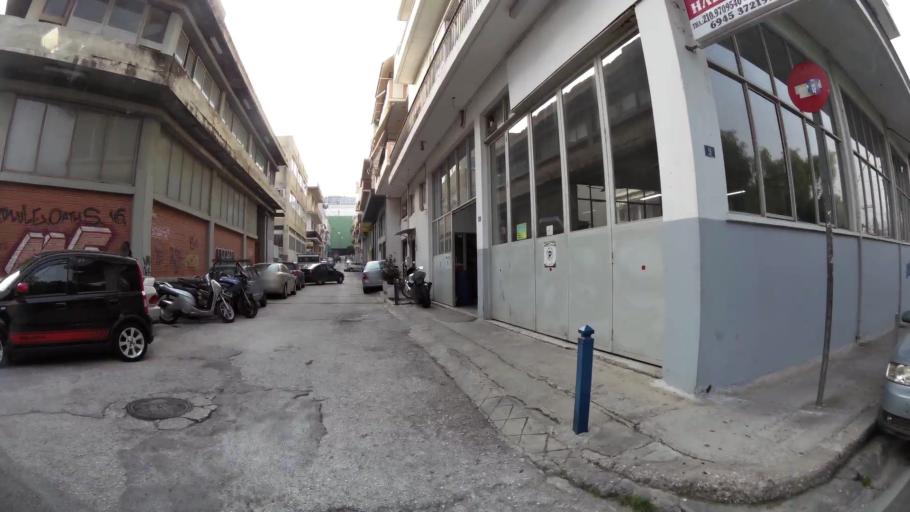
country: GR
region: Attica
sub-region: Nomarchia Athinas
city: Agios Dimitrios
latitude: 37.9411
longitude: 23.7388
